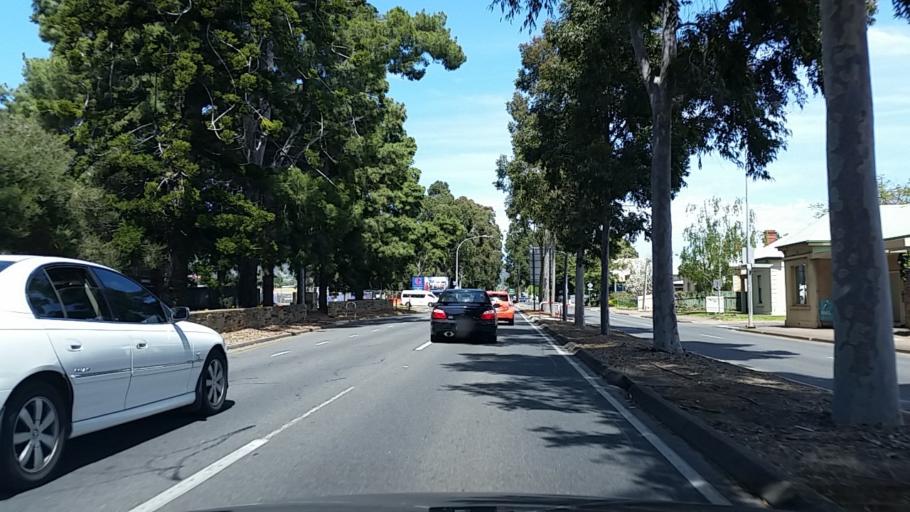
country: AU
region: South Australia
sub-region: Unley
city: Fullarton
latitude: -34.9423
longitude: 138.6248
